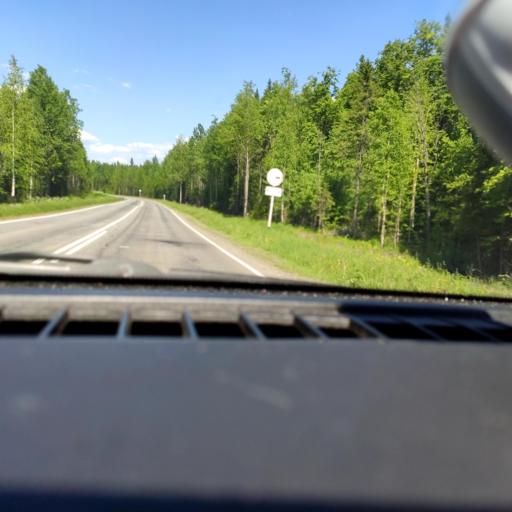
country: RU
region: Perm
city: Polazna
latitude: 58.2615
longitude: 56.1670
